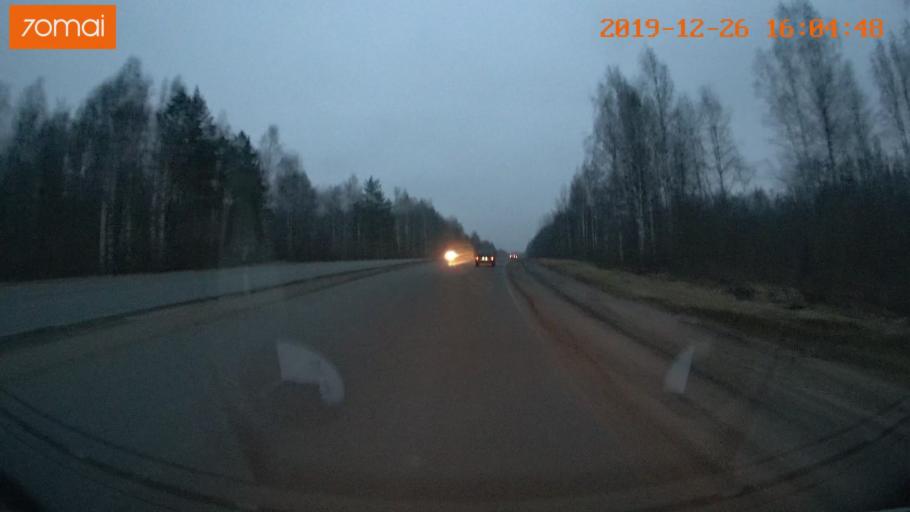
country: RU
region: Jaroslavl
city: Rybinsk
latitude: 58.0084
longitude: 38.8794
